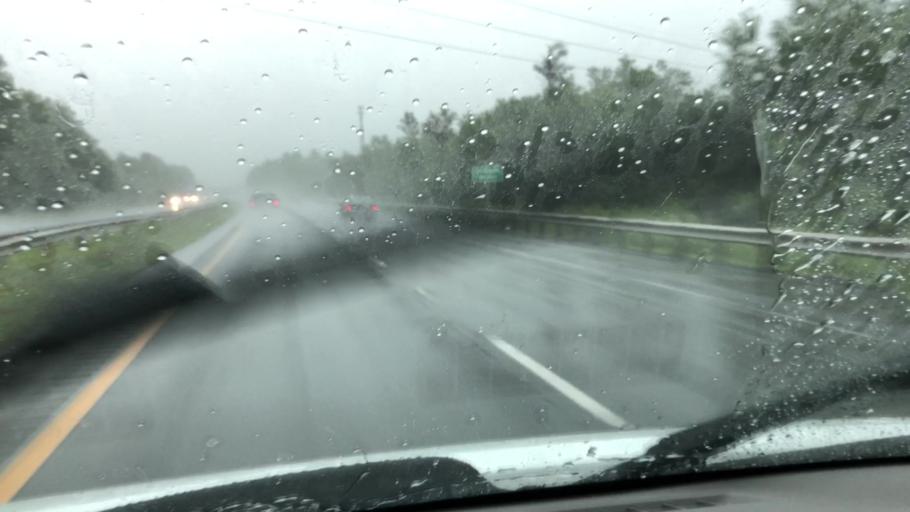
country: US
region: Massachusetts
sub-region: Berkshire County
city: Otis
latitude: 42.2451
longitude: -73.0929
